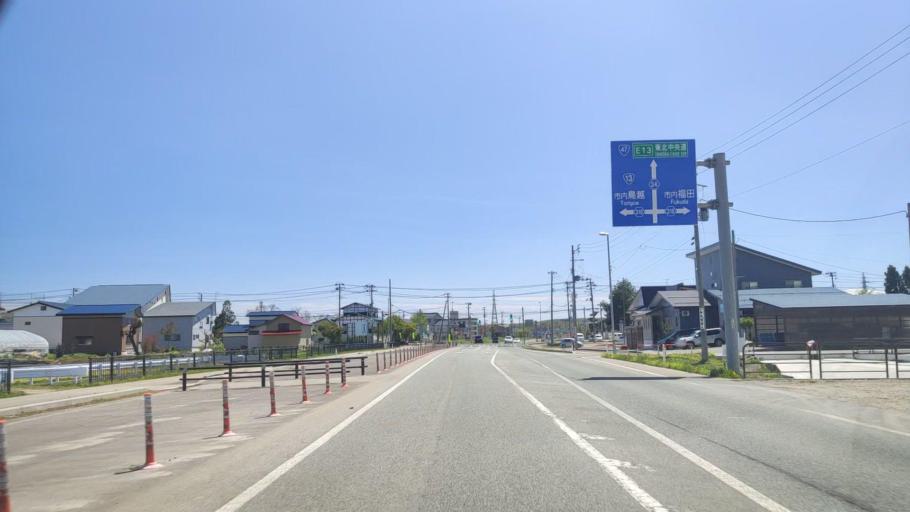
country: JP
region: Yamagata
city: Shinjo
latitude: 38.7514
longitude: 140.2950
